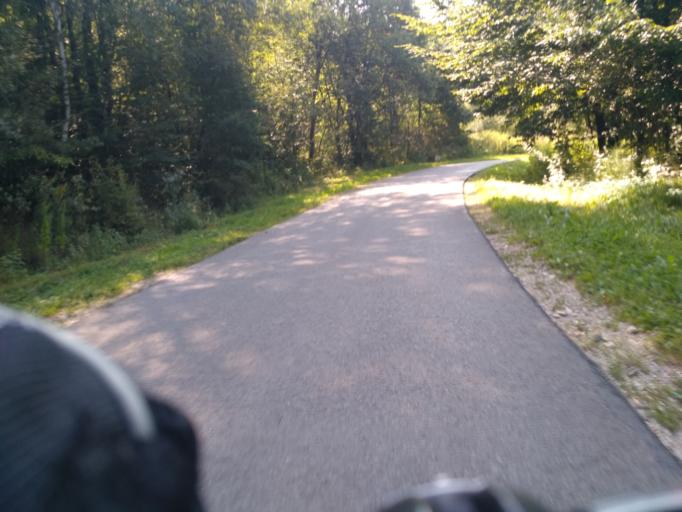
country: PL
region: Subcarpathian Voivodeship
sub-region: Powiat brzozowski
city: Golcowa
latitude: 49.7902
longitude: 22.0237
